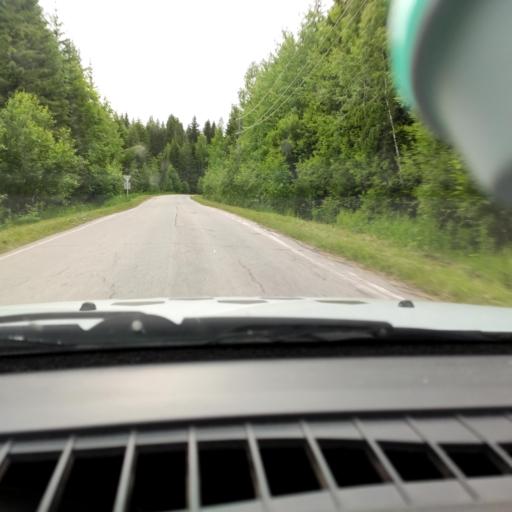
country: RU
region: Perm
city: Lys'va
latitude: 58.1148
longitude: 57.7007
